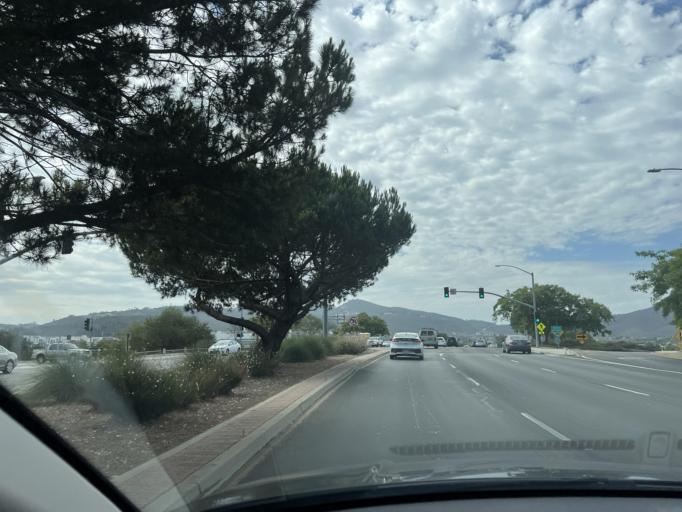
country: US
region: California
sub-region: San Diego County
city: San Marcos
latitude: 33.1387
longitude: -117.1638
